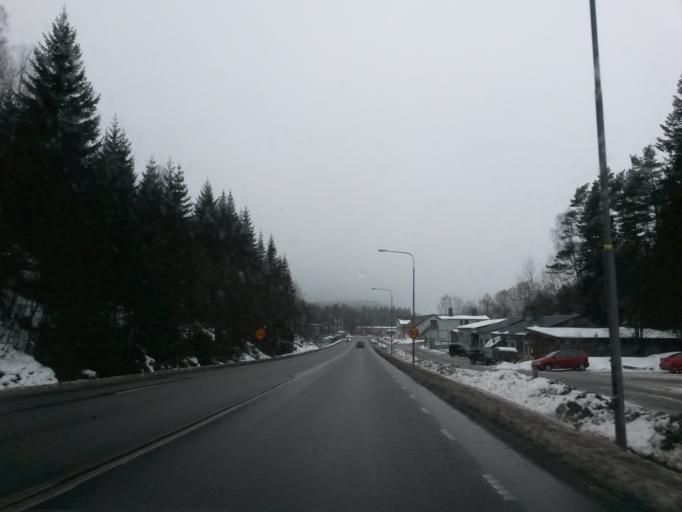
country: SE
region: Vaestra Goetaland
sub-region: Boras Kommun
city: Ganghester
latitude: 57.6965
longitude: 13.0346
